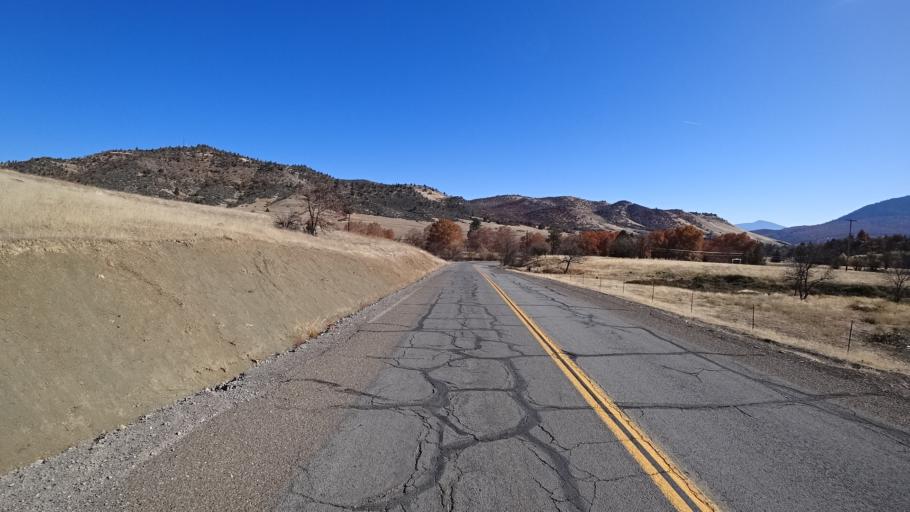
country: US
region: California
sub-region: Siskiyou County
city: Yreka
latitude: 41.9202
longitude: -122.5695
